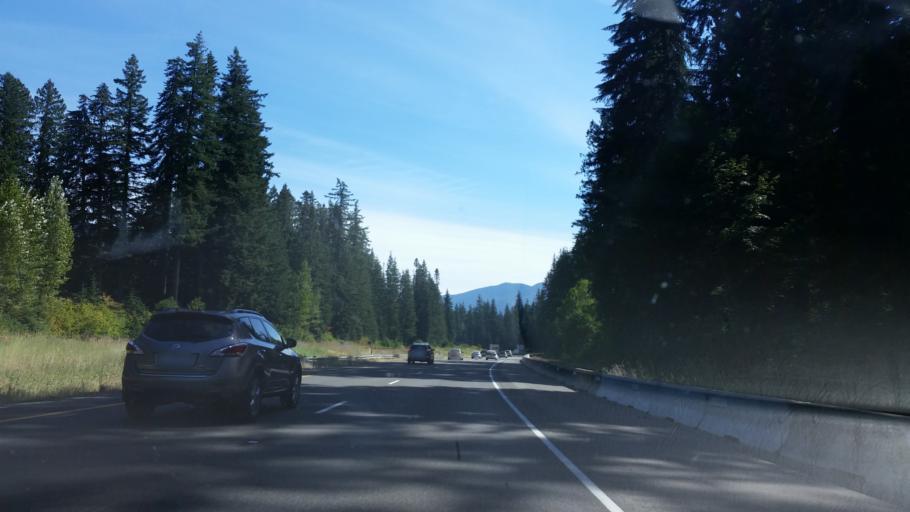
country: US
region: Washington
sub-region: Kittitas County
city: Cle Elum
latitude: 47.3138
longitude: -121.3154
